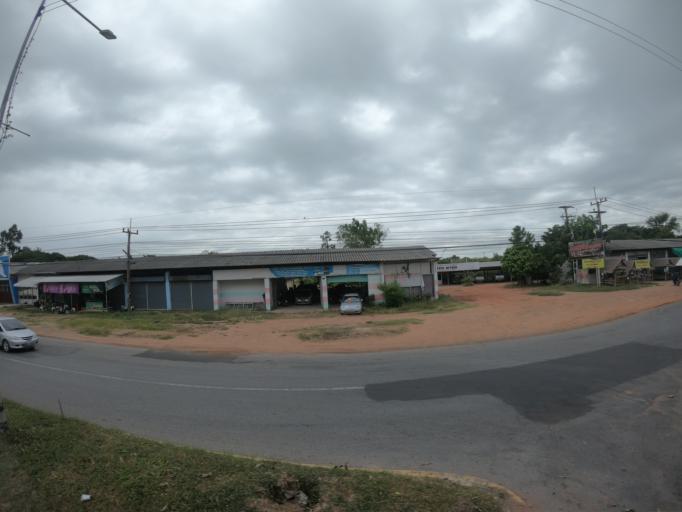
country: TH
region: Maha Sarakham
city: Maha Sarakham
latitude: 16.1687
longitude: 103.2899
